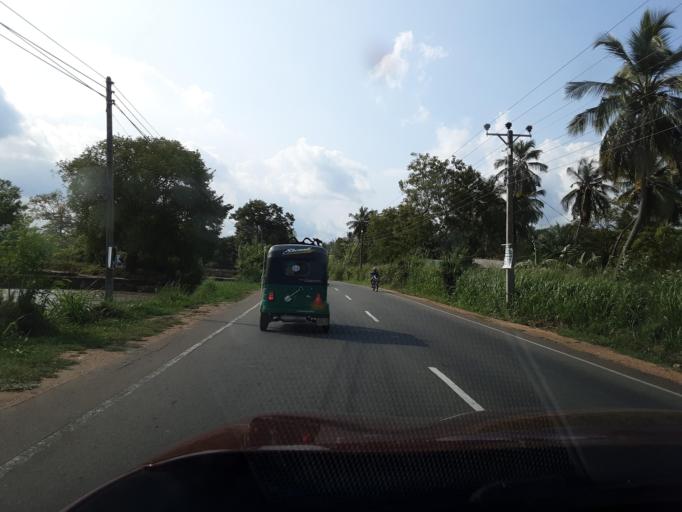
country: LK
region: Uva
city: Haputale
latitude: 6.5977
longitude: 81.1414
